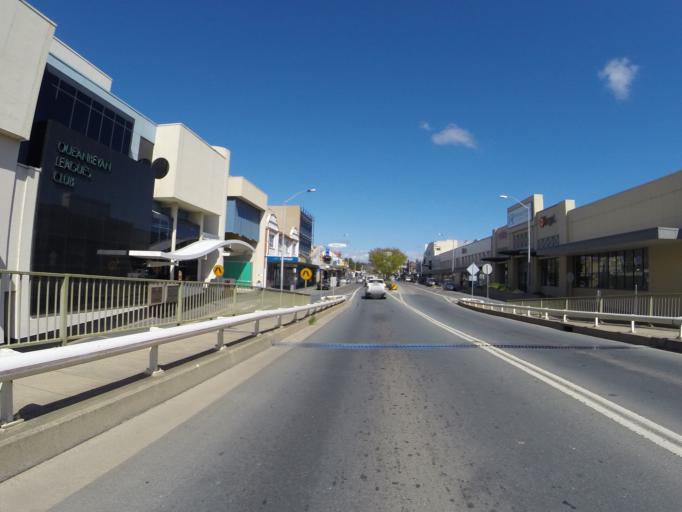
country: AU
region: New South Wales
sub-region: Queanbeyan
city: Queanbeyan
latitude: -35.3523
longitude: 149.2365
